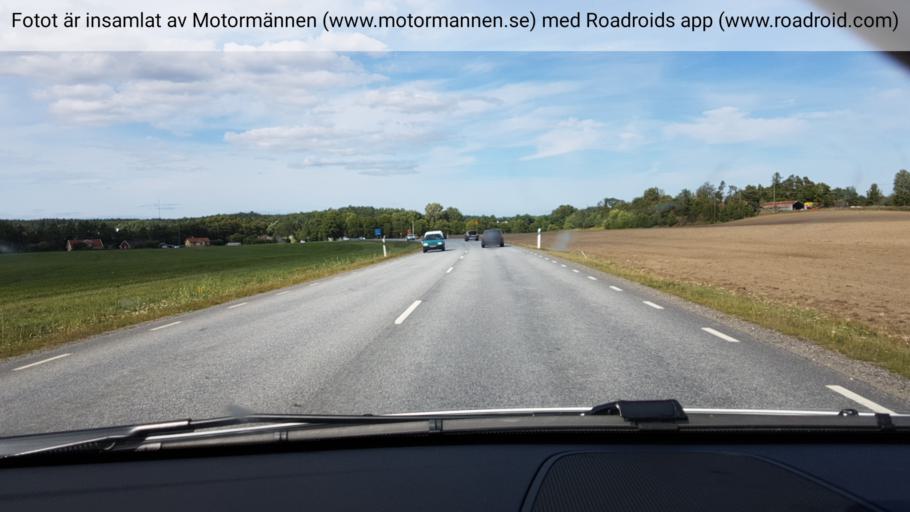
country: SE
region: Stockholm
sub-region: Sodertalje Kommun
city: Pershagen
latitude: 59.0774
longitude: 17.6076
